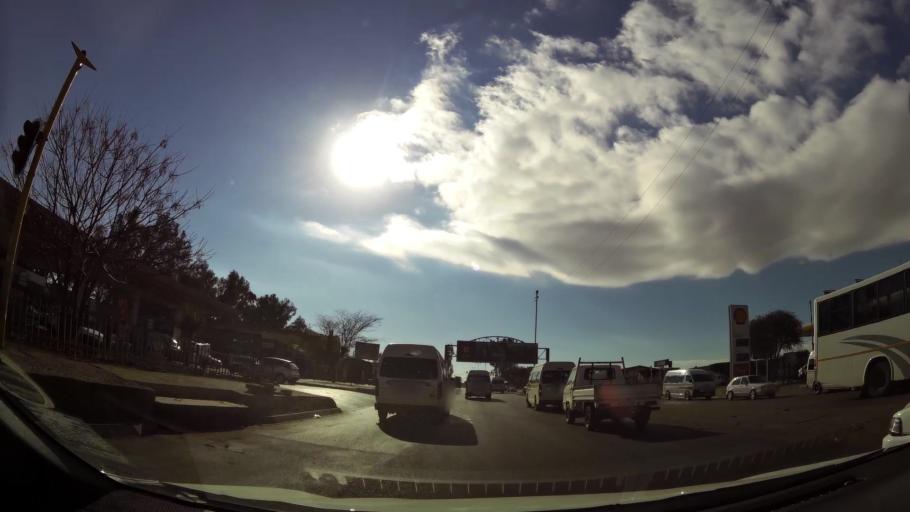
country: ZA
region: Gauteng
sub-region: City of Tshwane Metropolitan Municipality
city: Cullinan
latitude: -25.7140
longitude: 28.3749
